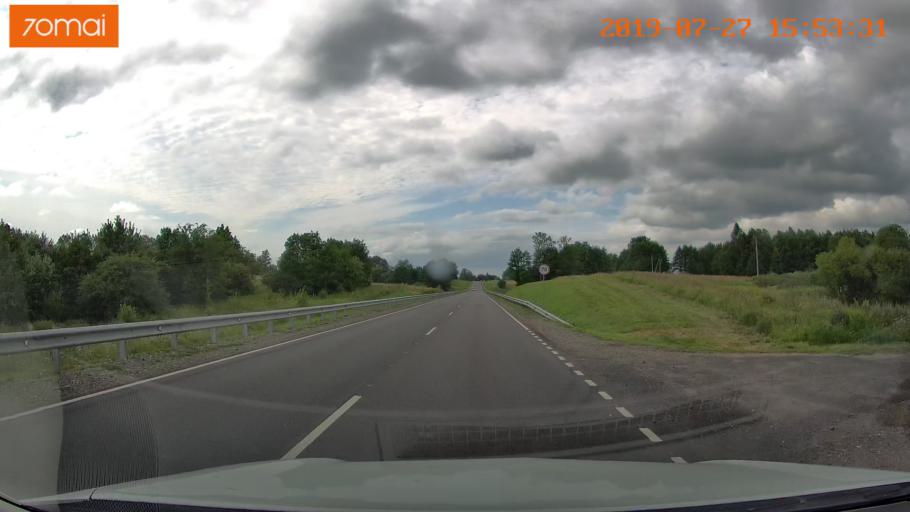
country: RU
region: Kaliningrad
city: Chernyakhovsk
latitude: 54.6038
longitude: 21.9528
